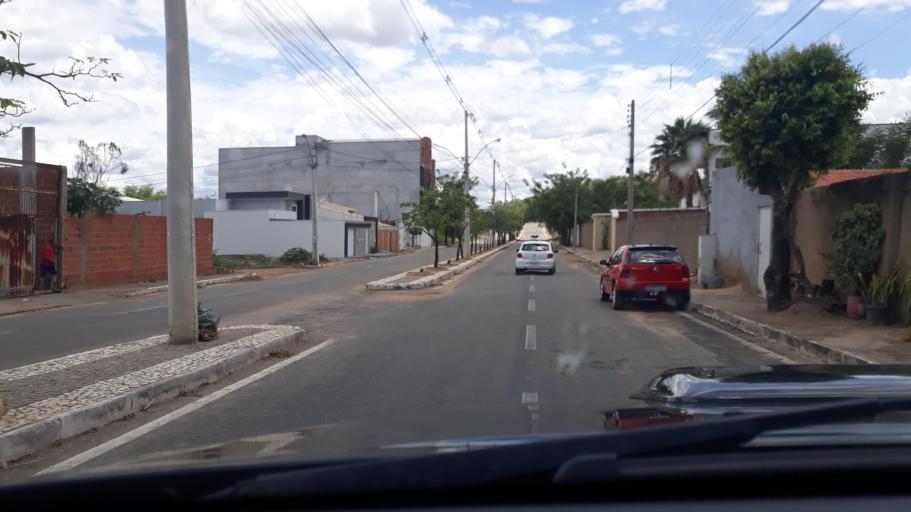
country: BR
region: Bahia
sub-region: Guanambi
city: Guanambi
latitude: -14.2266
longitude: -42.7685
